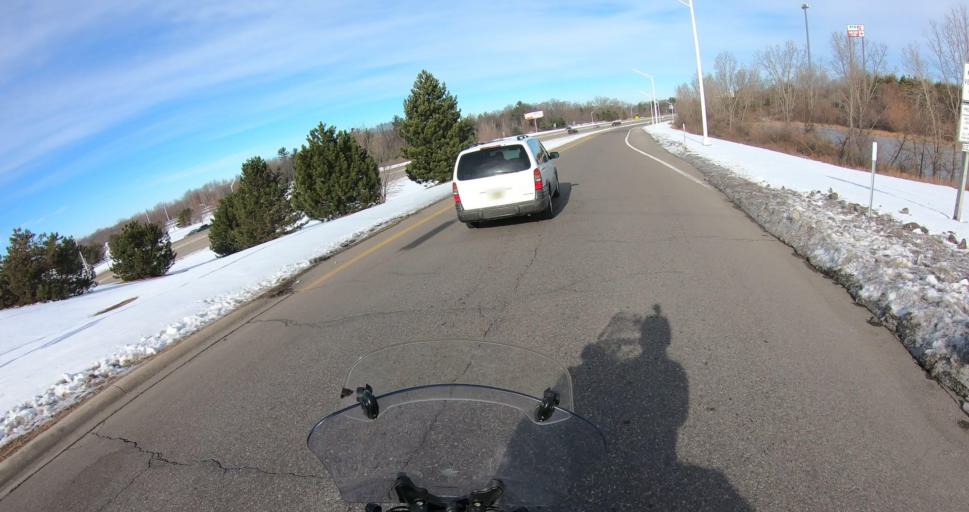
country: US
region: Michigan
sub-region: Genesee County
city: Clio
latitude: 43.1811
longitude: -83.7655
